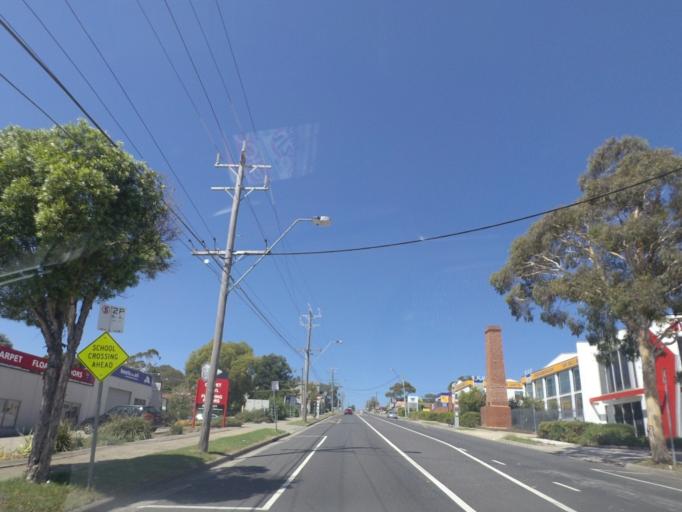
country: AU
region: Victoria
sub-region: Banyule
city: Montmorency
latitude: -37.7108
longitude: 145.1173
